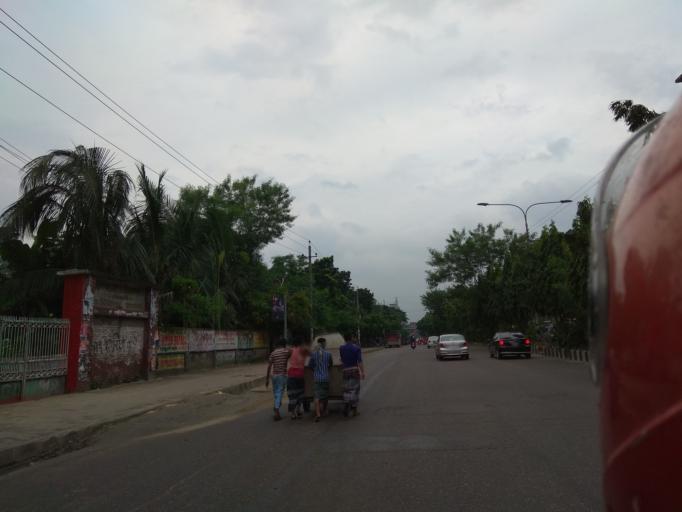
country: BD
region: Dhaka
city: Azimpur
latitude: 23.7493
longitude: 90.3793
